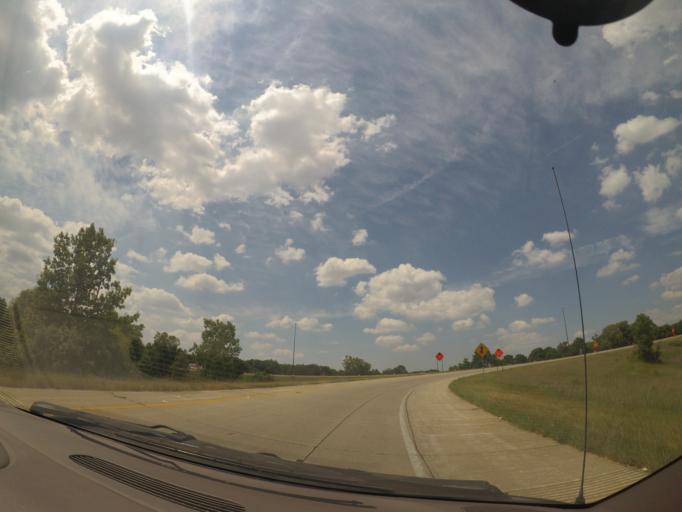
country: US
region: Indiana
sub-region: Elkhart County
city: Dunlap
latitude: 41.6496
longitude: -85.9432
